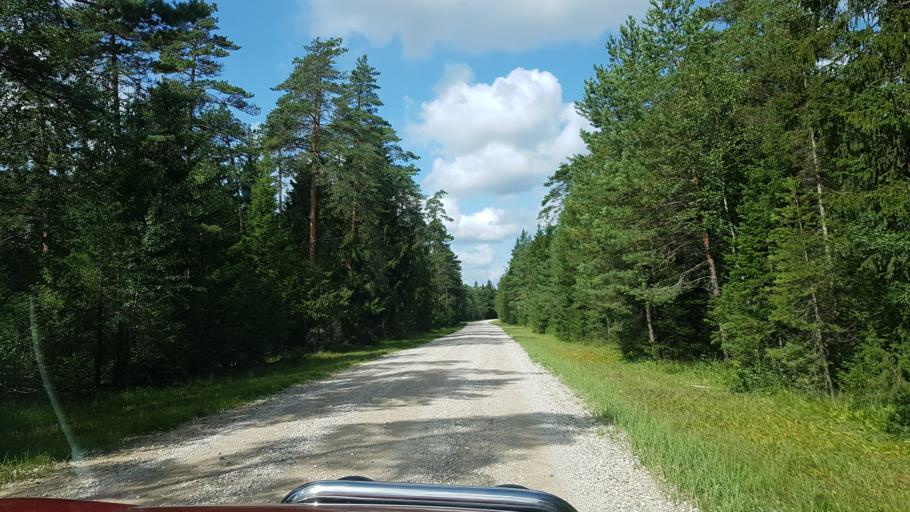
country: EE
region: Raplamaa
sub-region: Rapla vald
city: Rapla
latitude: 58.9621
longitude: 24.6432
